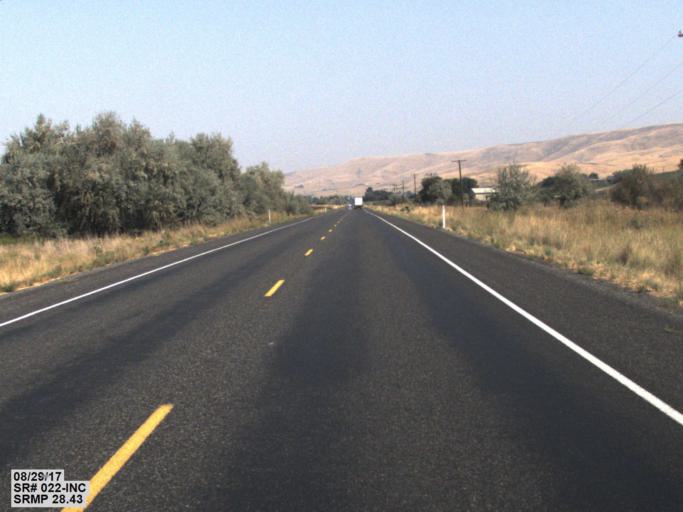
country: US
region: Washington
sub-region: Yakima County
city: Grandview
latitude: 46.1894
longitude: -119.8940
